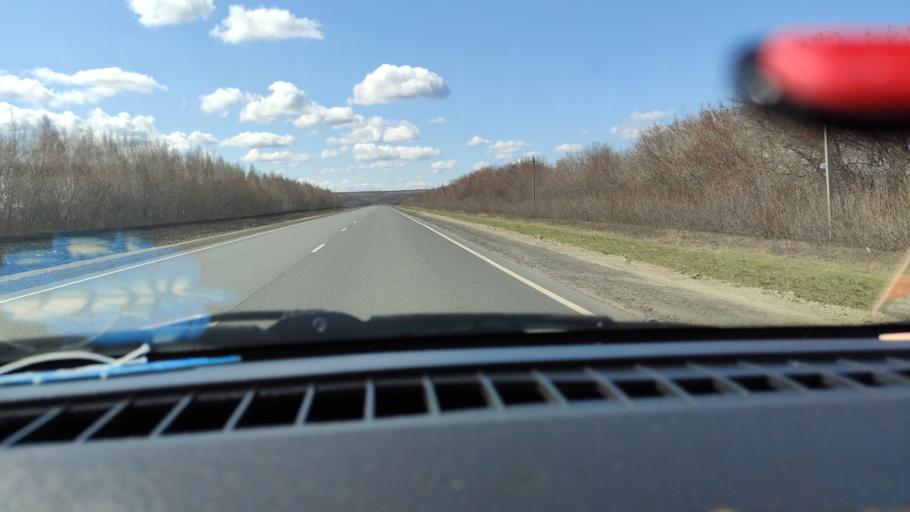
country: RU
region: Samara
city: Varlamovo
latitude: 52.9792
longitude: 48.3113
